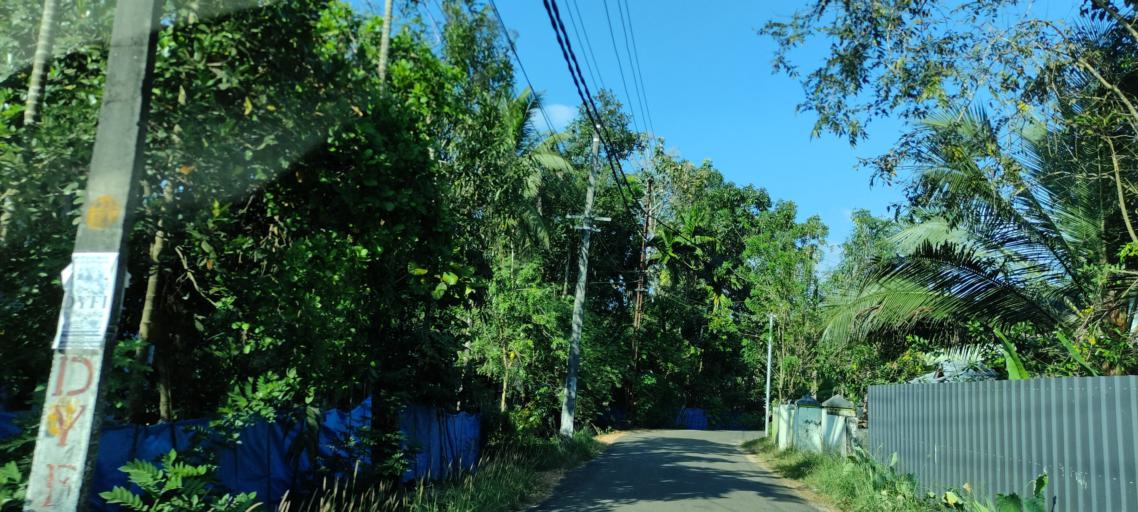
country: IN
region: Kerala
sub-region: Alappuzha
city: Shertallai
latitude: 9.6444
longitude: 76.3451
